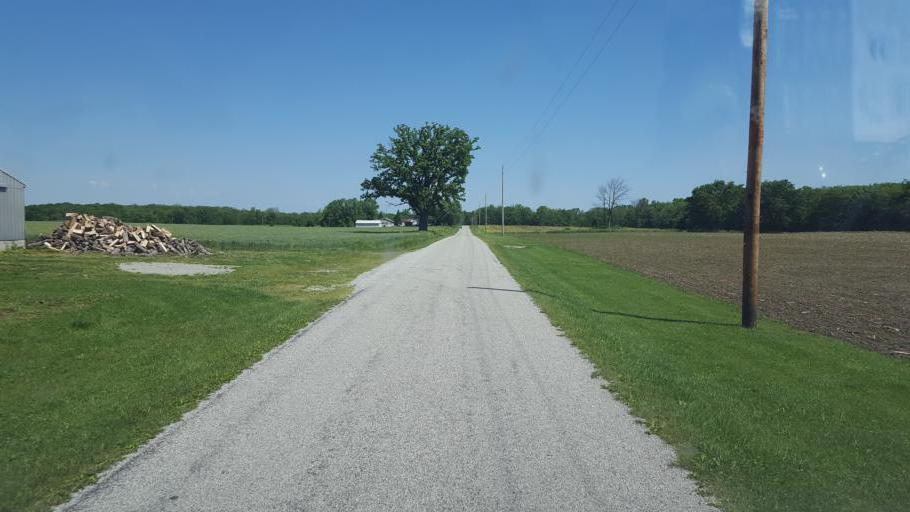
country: US
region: Ohio
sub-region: Hardin County
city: Forest
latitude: 40.6675
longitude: -83.3906
